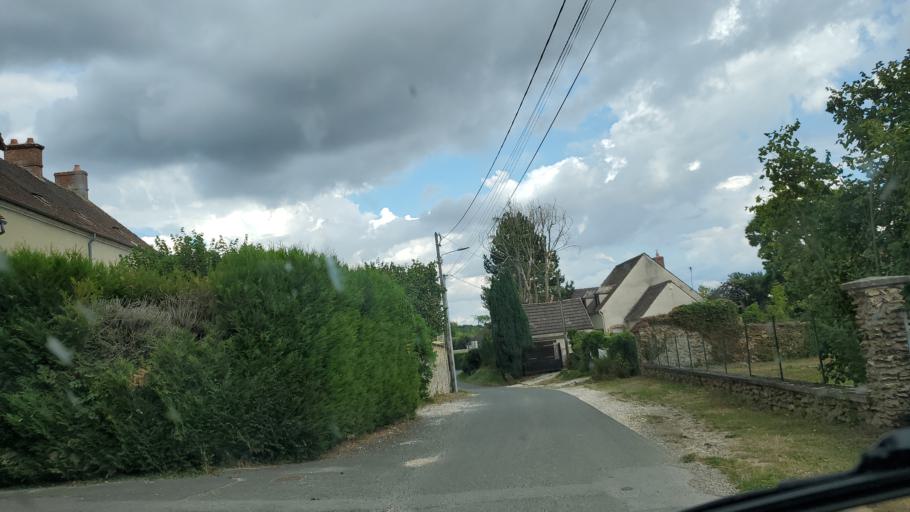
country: FR
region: Ile-de-France
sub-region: Departement de Seine-et-Marne
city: Chailly-en-Brie
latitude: 48.7769
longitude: 3.1612
